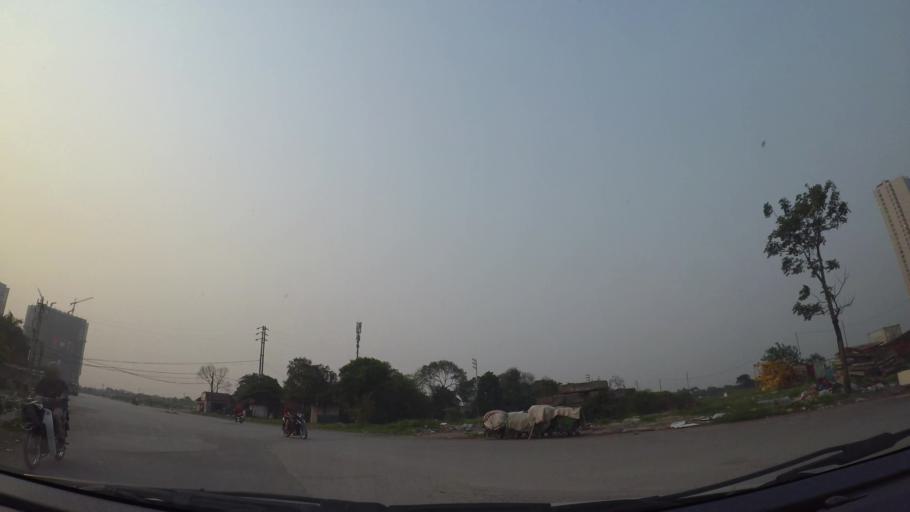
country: VN
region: Ha Noi
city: Cau Dien
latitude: 21.0069
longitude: 105.7266
